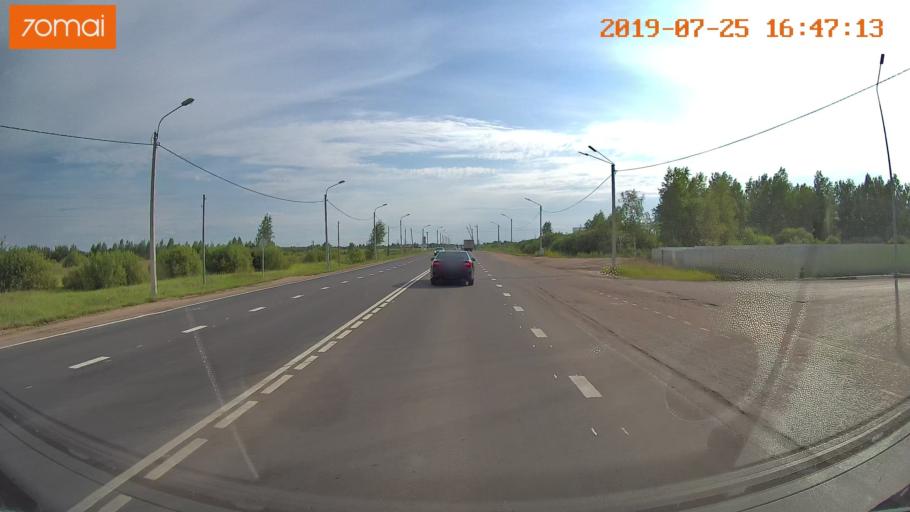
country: RU
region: Ivanovo
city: Privolzhsk
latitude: 57.3668
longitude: 41.2726
